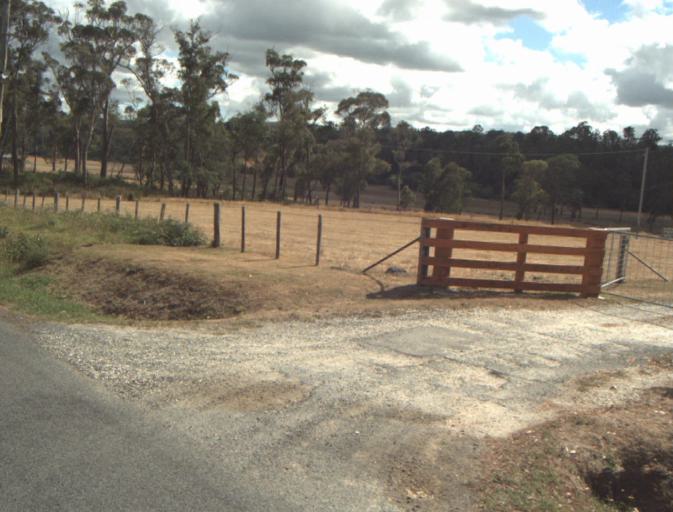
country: AU
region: Tasmania
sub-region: Launceston
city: Mayfield
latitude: -41.2308
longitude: 147.1454
